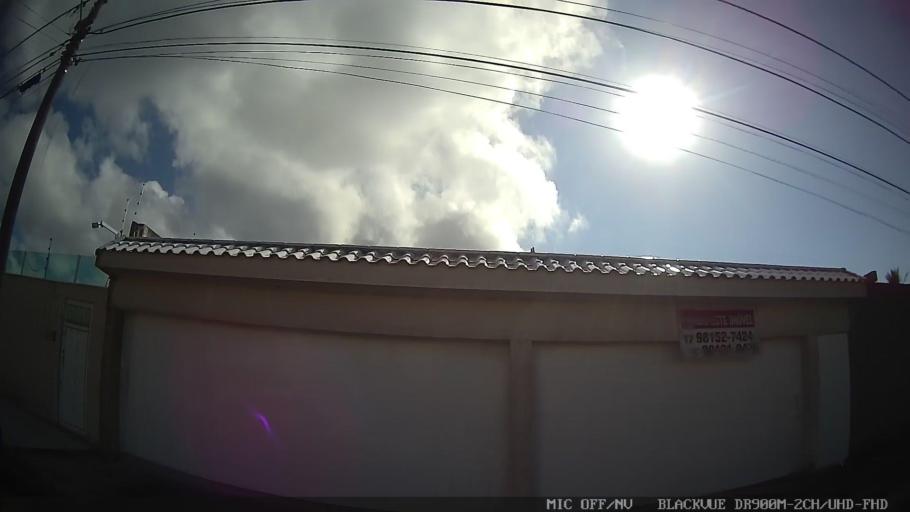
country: BR
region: Sao Paulo
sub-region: Peruibe
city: Peruibe
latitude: -24.2744
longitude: -46.9371
